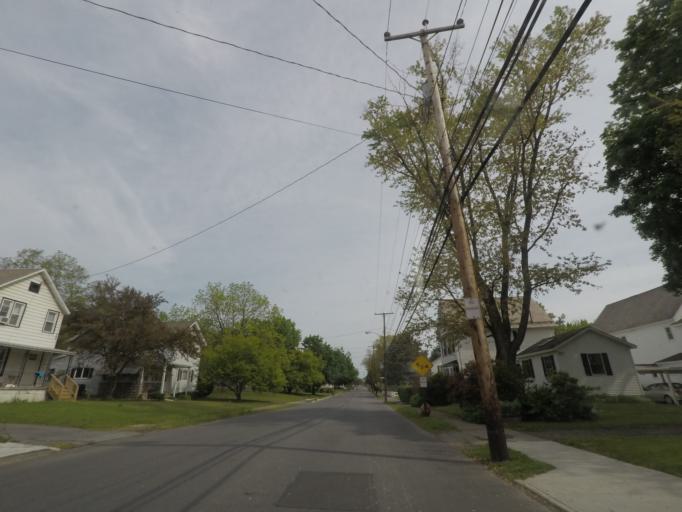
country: US
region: New York
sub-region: Saratoga County
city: Mechanicville
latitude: 42.8907
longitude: -73.6881
